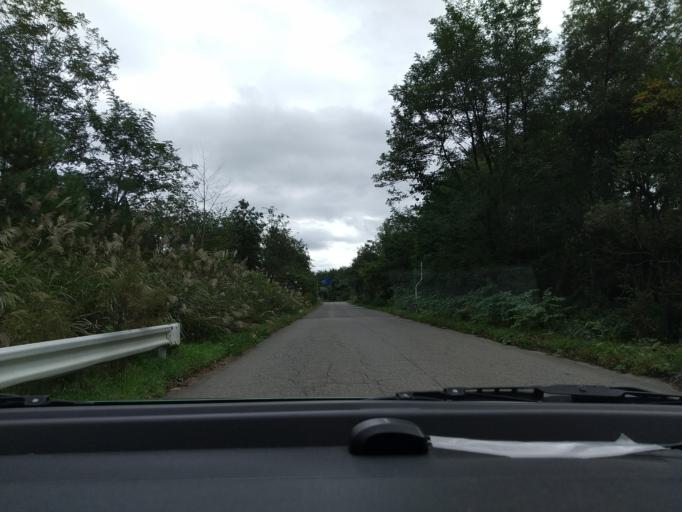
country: JP
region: Akita
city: Kakunodatemachi
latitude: 39.5778
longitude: 140.6288
